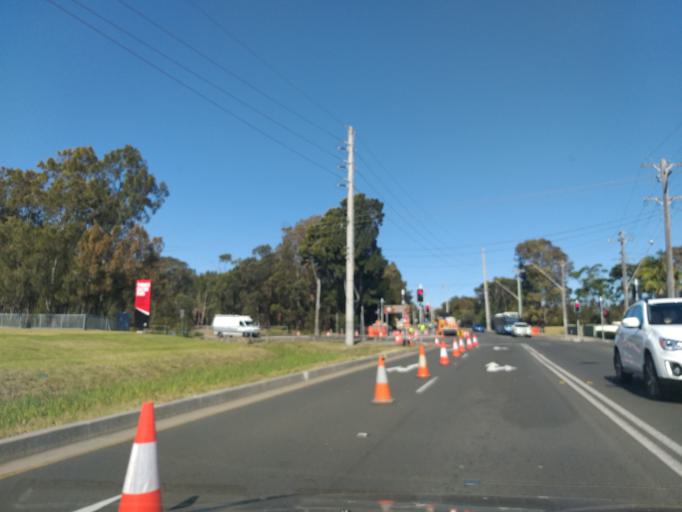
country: AU
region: New South Wales
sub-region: Wollongong
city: Fairy Meadow
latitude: -34.3957
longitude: 150.9010
